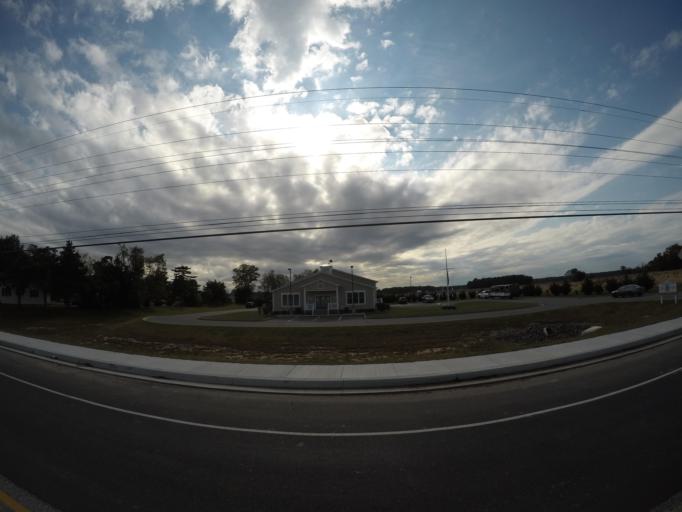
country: US
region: Delaware
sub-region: Sussex County
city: Lewes
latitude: 38.7253
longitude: -75.1443
